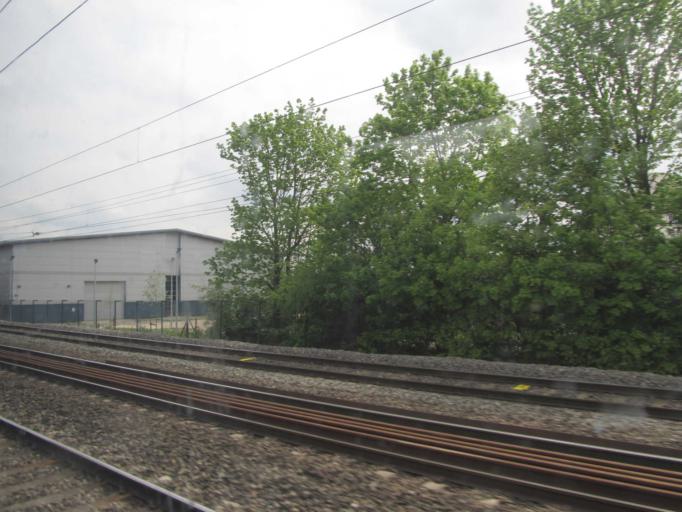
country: GB
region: England
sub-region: Greater London
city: Hayes
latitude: 51.5028
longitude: -0.4143
